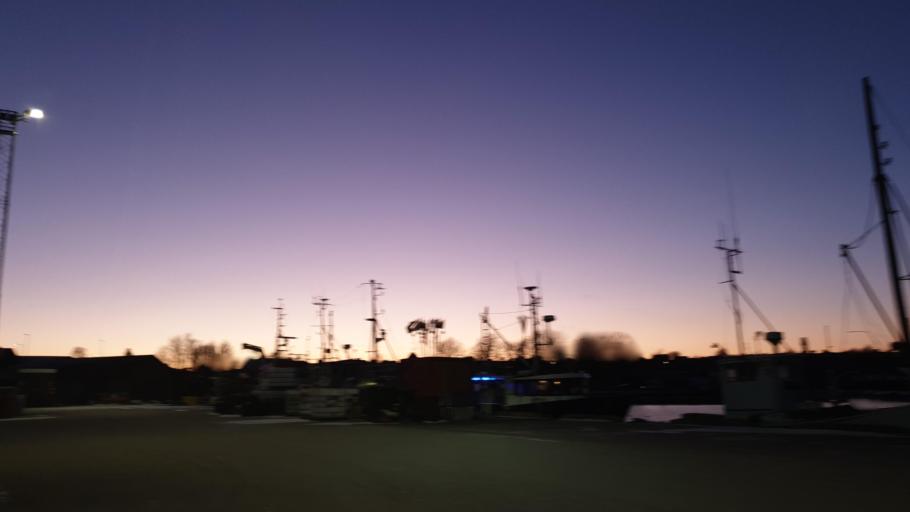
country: SE
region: Gotland
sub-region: Gotland
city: Slite
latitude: 57.4219
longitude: 18.9162
